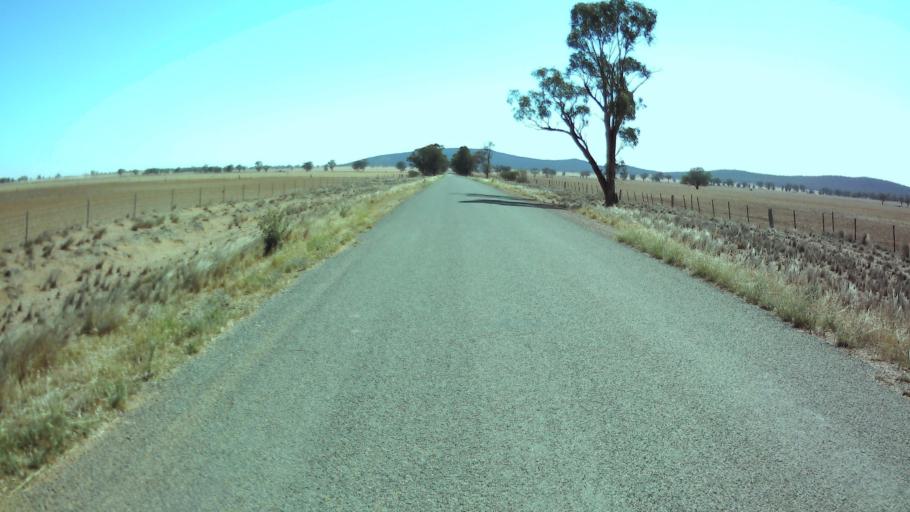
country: AU
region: New South Wales
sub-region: Weddin
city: Grenfell
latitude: -33.7123
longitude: 147.9098
